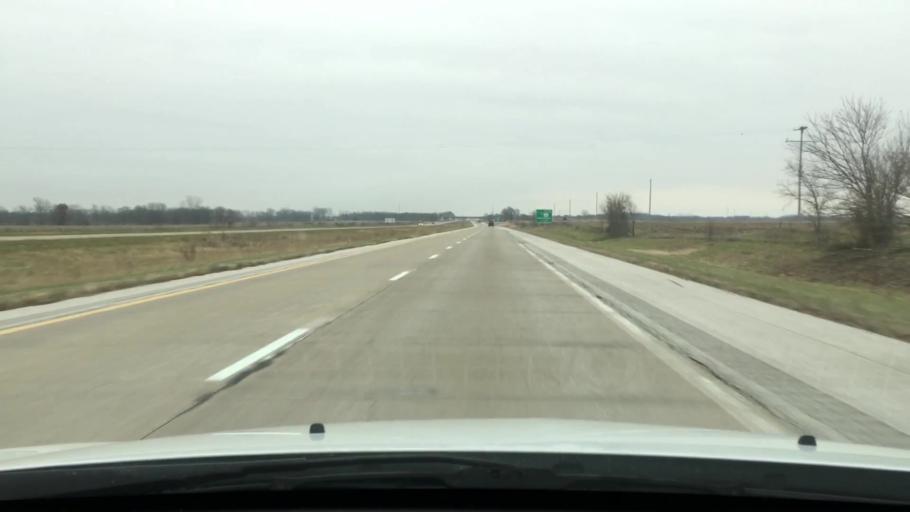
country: US
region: Illinois
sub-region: Scott County
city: Winchester
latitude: 39.6809
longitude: -90.4739
